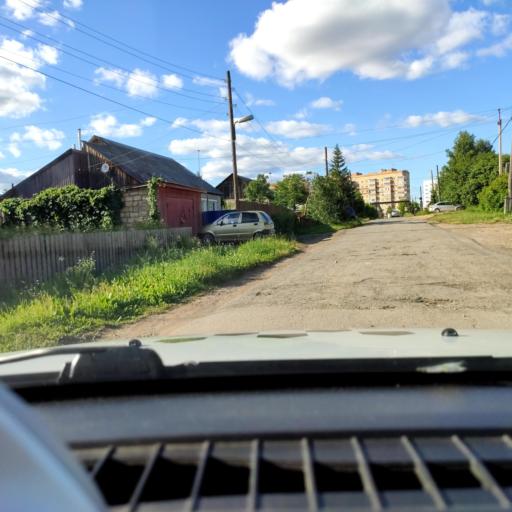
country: RU
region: Perm
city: Froly
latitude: 57.9177
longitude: 56.2758
